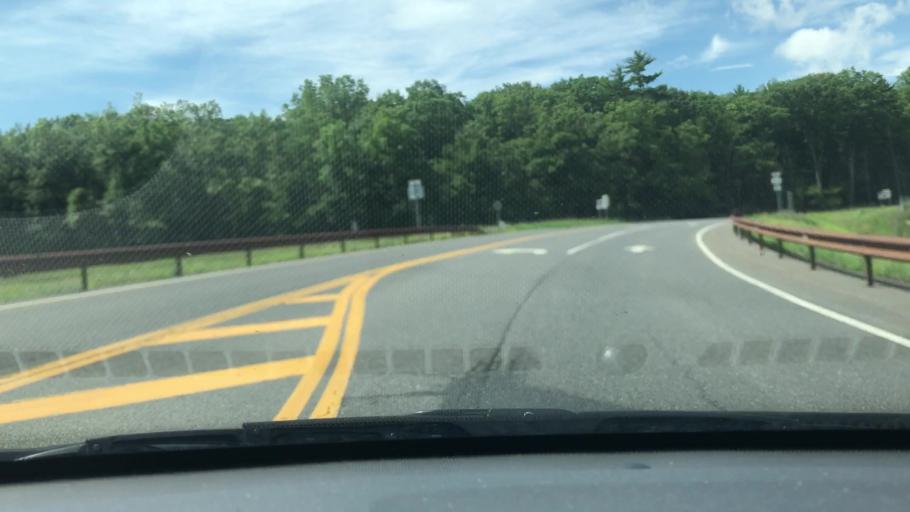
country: US
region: New York
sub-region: Ulster County
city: Shokan
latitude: 41.9339
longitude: -74.2186
